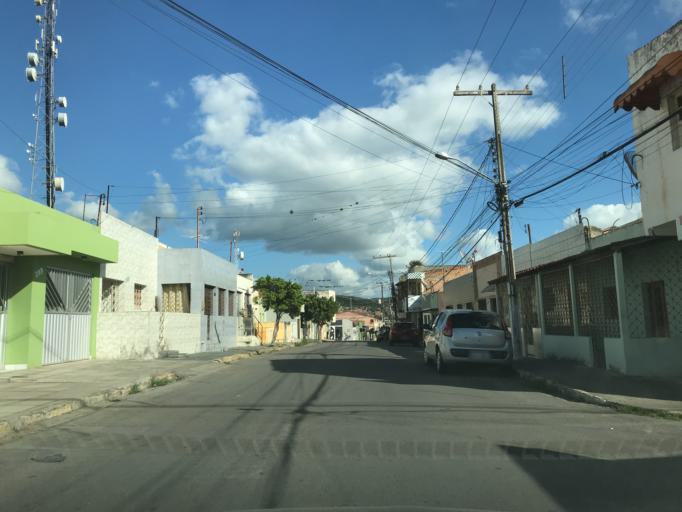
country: BR
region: Pernambuco
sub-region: Bezerros
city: Bezerros
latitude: -8.2422
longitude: -35.7548
